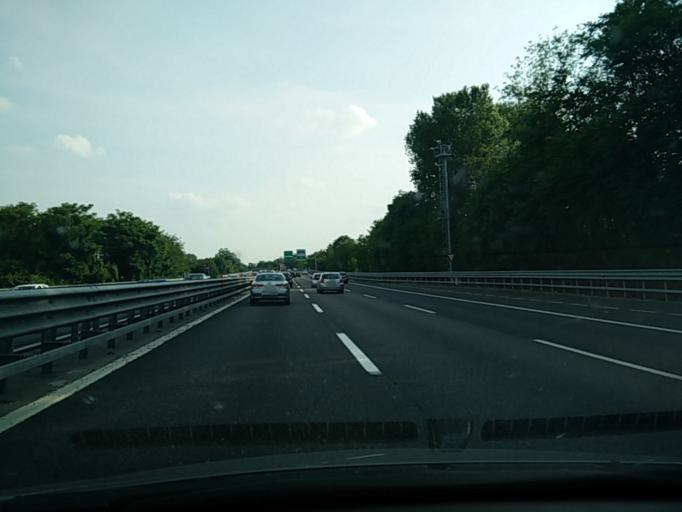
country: IT
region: Lombardy
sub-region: Citta metropolitana di Milano
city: Figino
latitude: 45.4692
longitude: 9.0784
